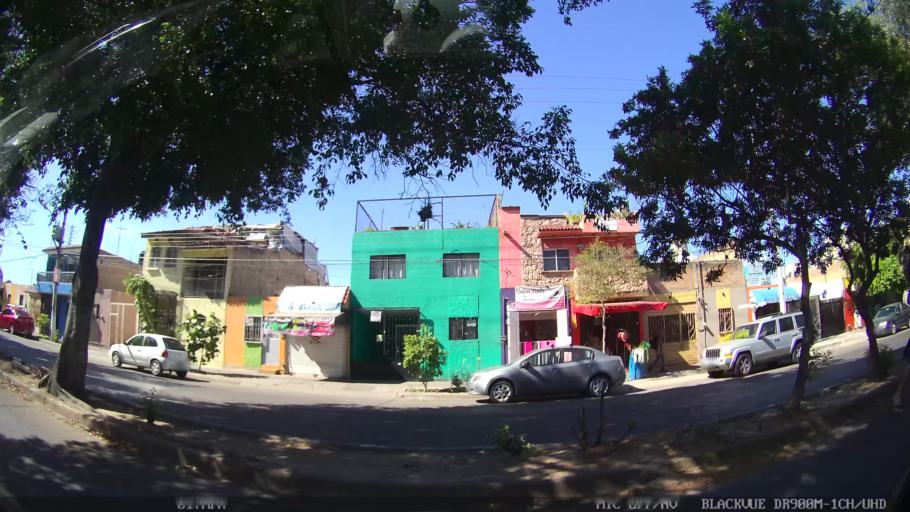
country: MX
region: Jalisco
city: Tlaquepaque
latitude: 20.6792
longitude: -103.2782
